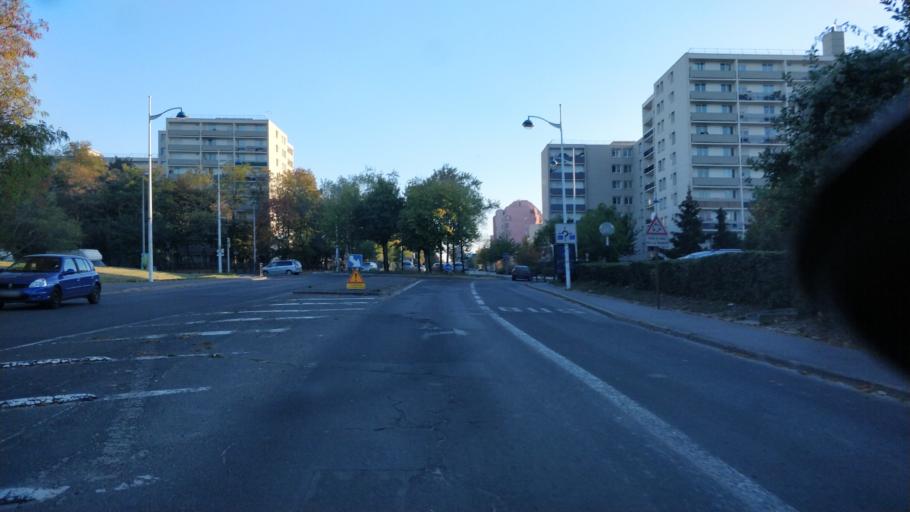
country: FR
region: Ile-de-France
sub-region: Departement de Seine-Saint-Denis
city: Gournay-sur-Marne
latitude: 48.8494
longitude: 2.5854
